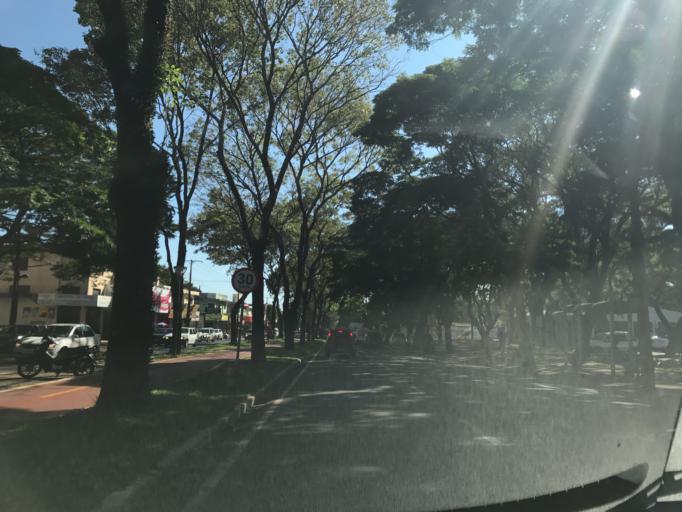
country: BR
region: Parana
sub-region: Maringa
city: Maringa
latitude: -23.4102
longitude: -51.9557
